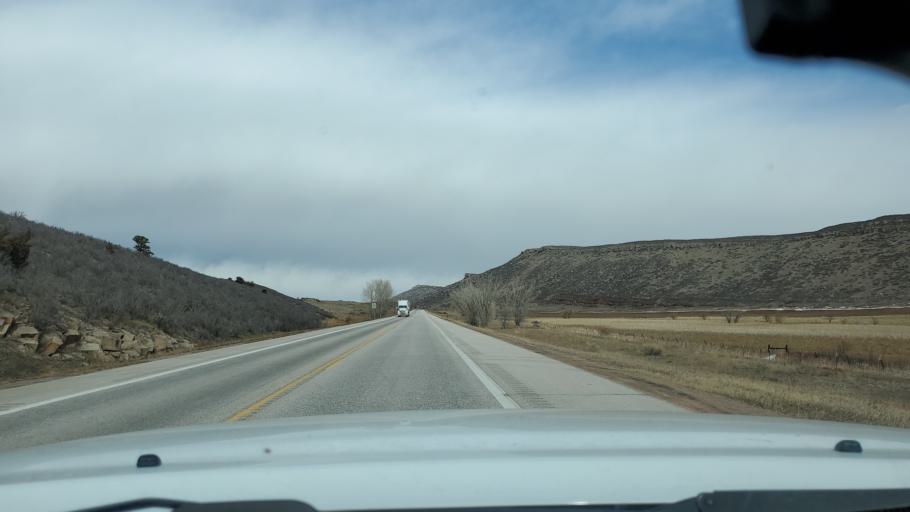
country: US
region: Colorado
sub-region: Larimer County
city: Laporte
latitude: 40.6835
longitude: -105.1758
